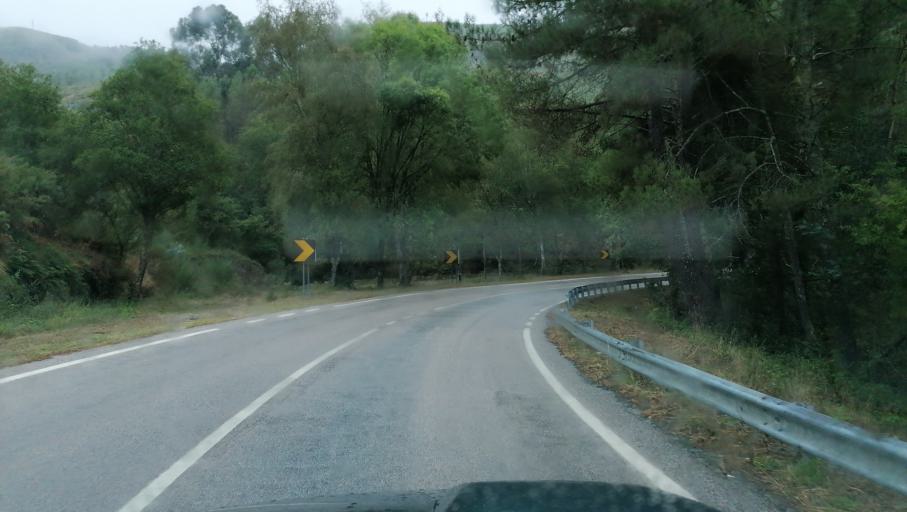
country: PT
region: Vila Real
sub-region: Ribeira de Pena
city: Ribeira de Pena
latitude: 41.5131
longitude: -7.8170
